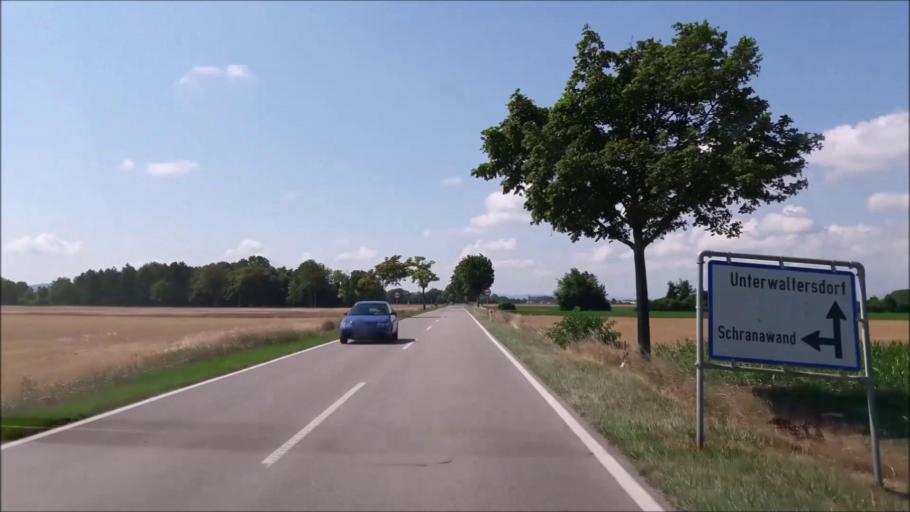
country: AT
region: Lower Austria
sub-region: Politischer Bezirk Baden
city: Mitterndorf an der Fischa
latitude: 47.9826
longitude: 16.4369
